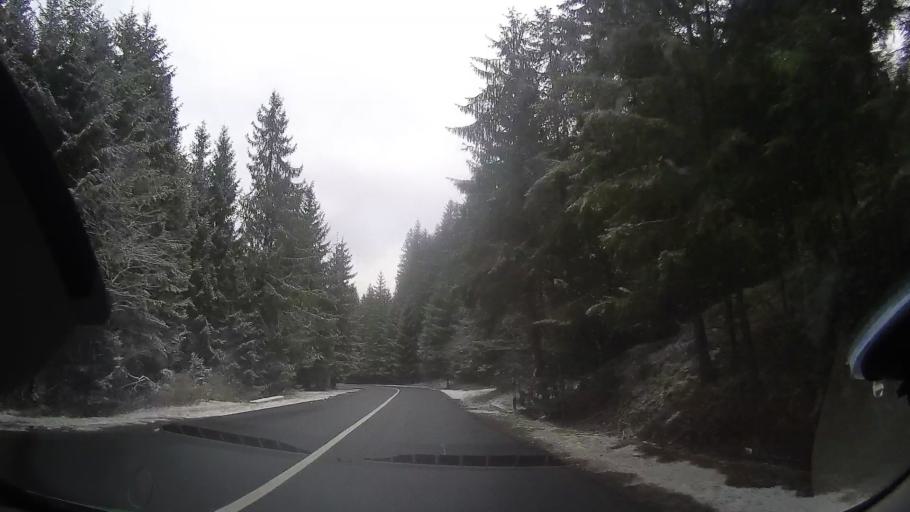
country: RO
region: Cluj
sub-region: Comuna Calatele
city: Calatele
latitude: 46.7326
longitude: 23.0401
